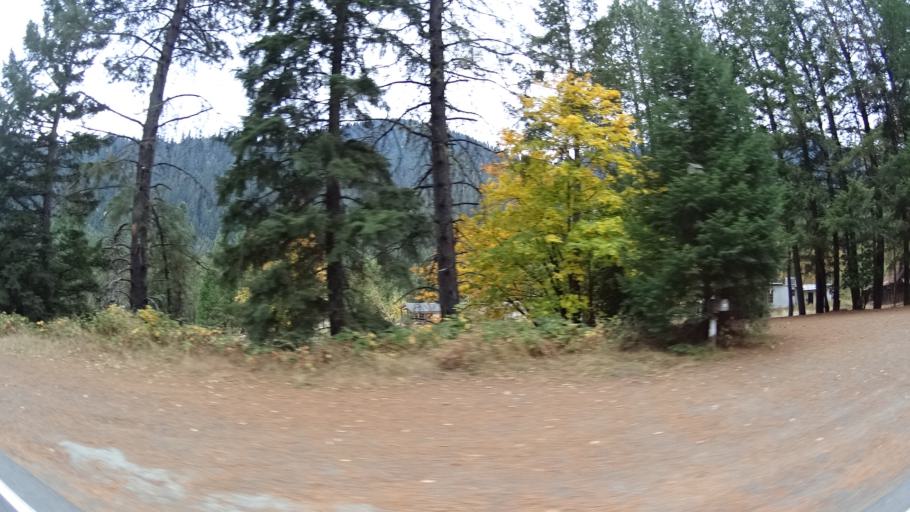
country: US
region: California
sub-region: Siskiyou County
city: Happy Camp
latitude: 41.8588
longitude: -123.4019
